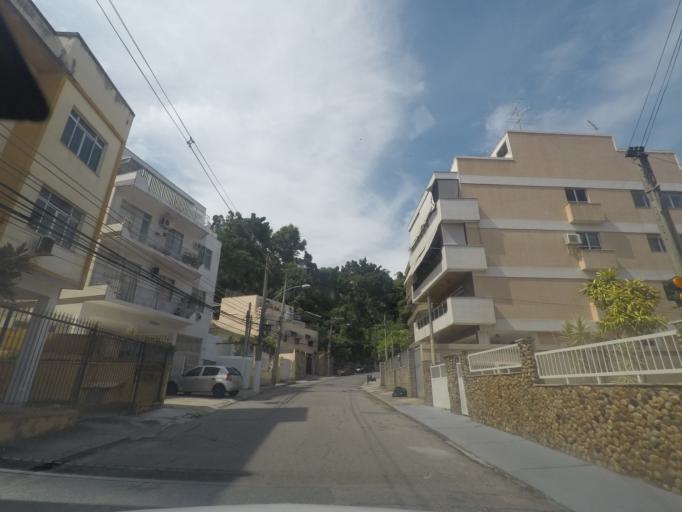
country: BR
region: Rio de Janeiro
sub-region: Rio De Janeiro
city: Rio de Janeiro
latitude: -22.8158
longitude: -43.1978
